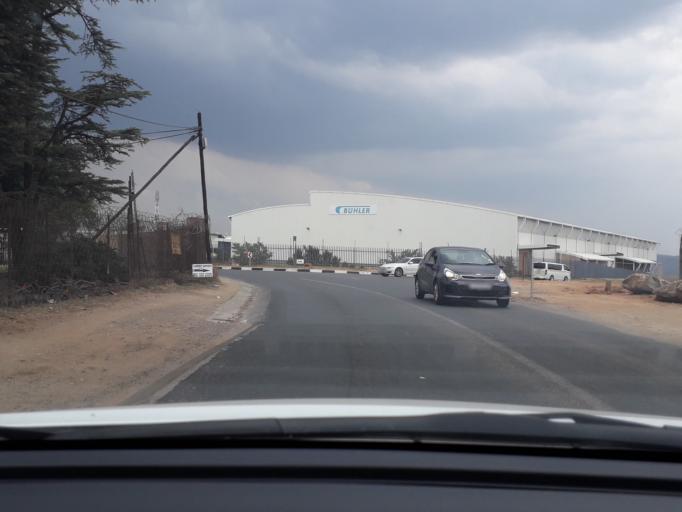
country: ZA
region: Gauteng
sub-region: West Rand District Municipality
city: Muldersdriseloop
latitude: -26.0713
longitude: 27.9232
